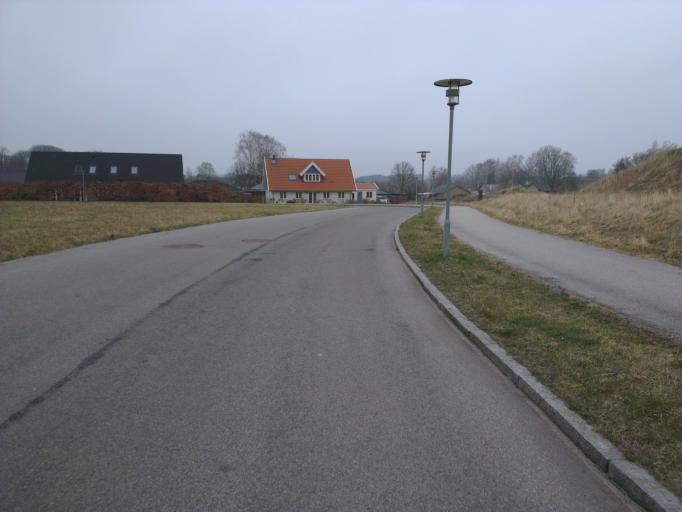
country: DK
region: Capital Region
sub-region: Frederikssund Kommune
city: Frederikssund
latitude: 55.8200
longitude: 12.0191
